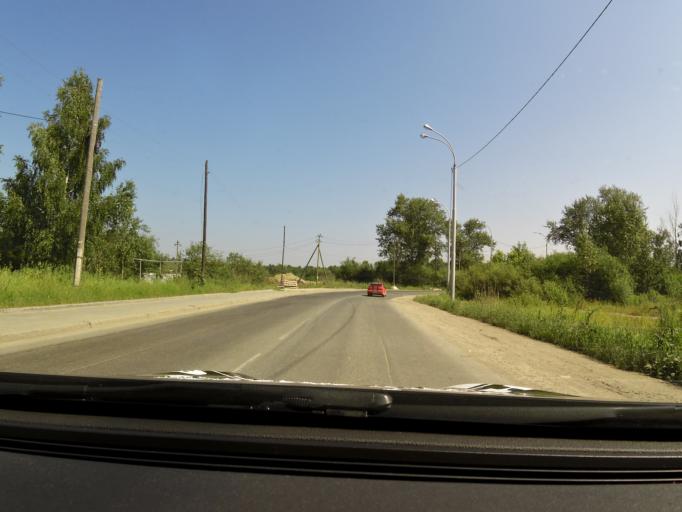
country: RU
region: Sverdlovsk
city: Shirokaya Rechka
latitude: 56.8081
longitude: 60.4973
